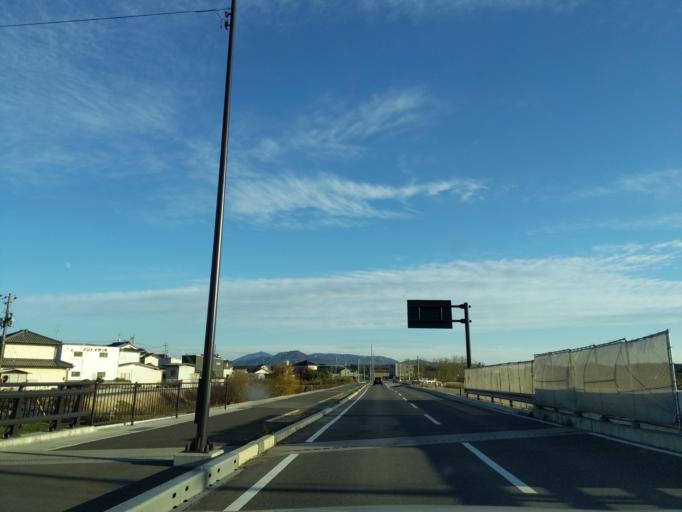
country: JP
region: Fukushima
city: Koriyama
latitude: 37.3563
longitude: 140.3783
